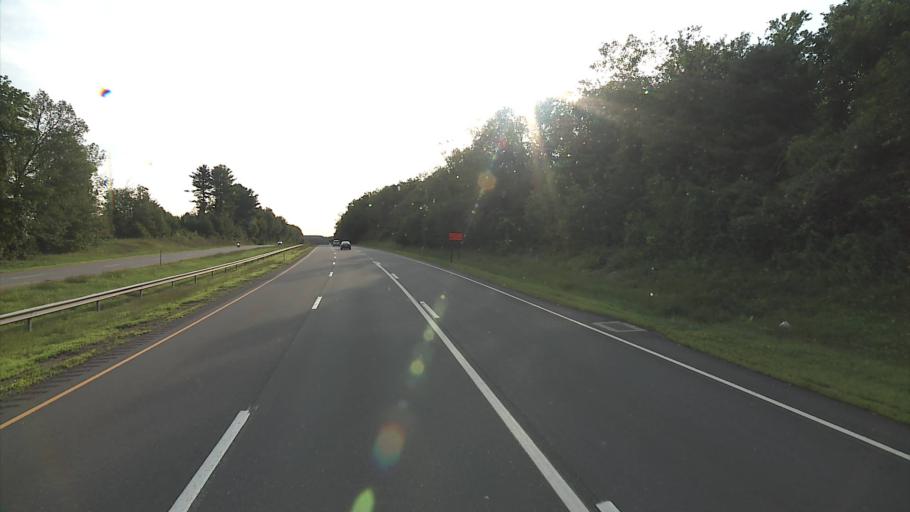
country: US
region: Connecticut
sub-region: New London County
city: Montville Center
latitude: 41.5611
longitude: -72.1540
